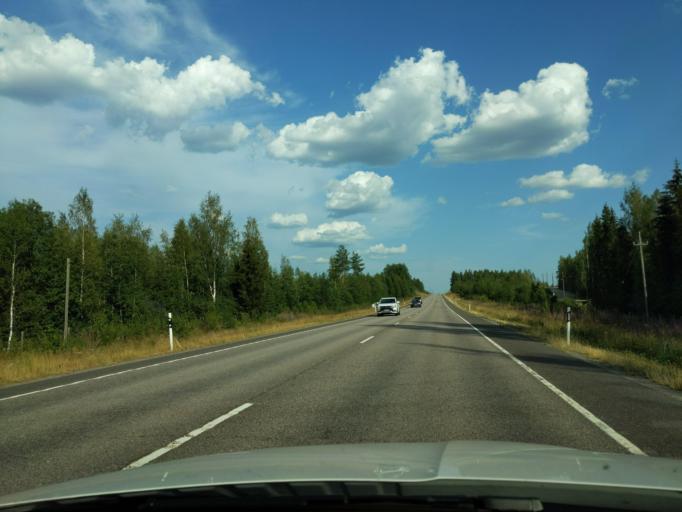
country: FI
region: Paijanne Tavastia
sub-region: Lahti
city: Hollola
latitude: 60.9924
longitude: 25.3743
